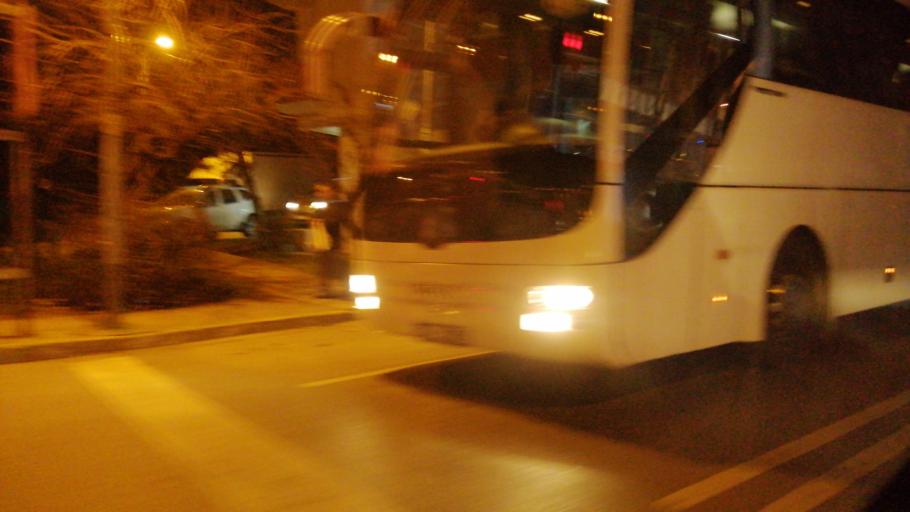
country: TR
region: Istanbul
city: Umraniye
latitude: 41.0085
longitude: 29.1265
